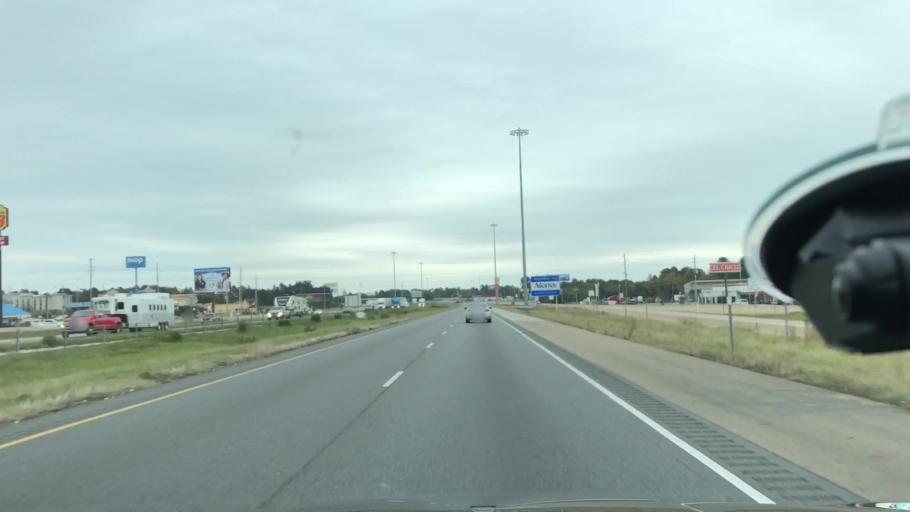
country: US
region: Arkansas
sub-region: Miller County
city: Texarkana
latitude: 33.4701
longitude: -94.0406
